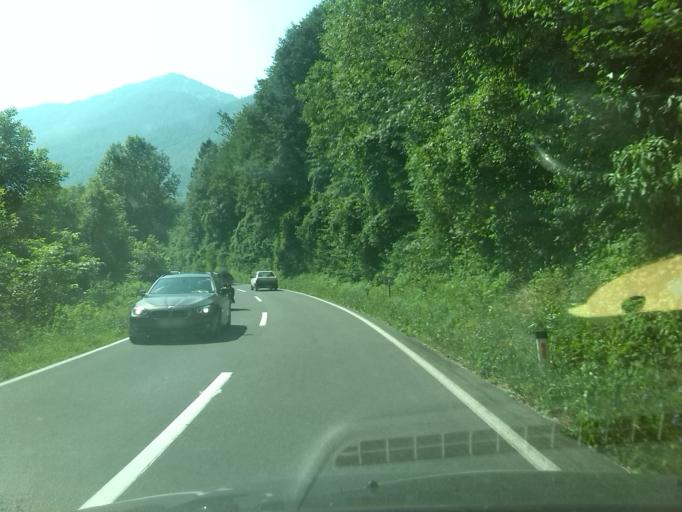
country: SI
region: Kobarid
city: Kobarid
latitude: 46.2285
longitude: 13.5957
